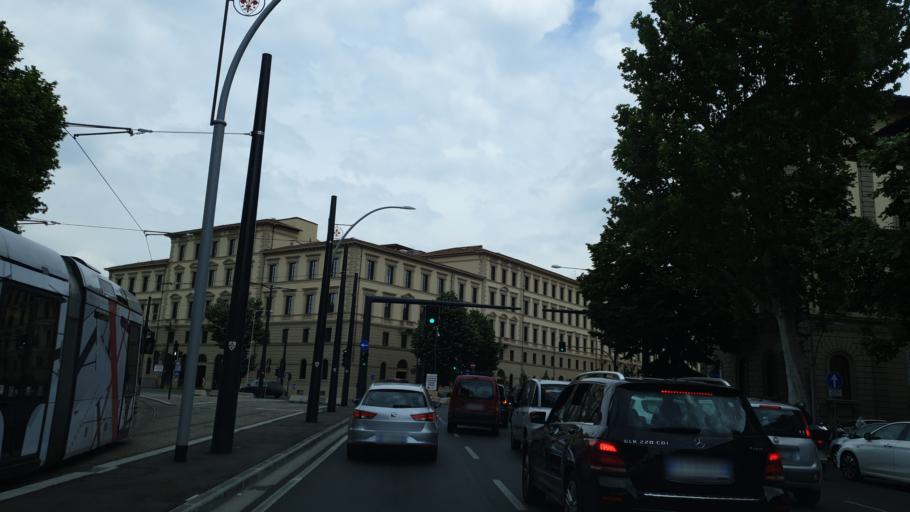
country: IT
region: Tuscany
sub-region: Province of Florence
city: Florence
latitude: 43.7813
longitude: 11.2524
